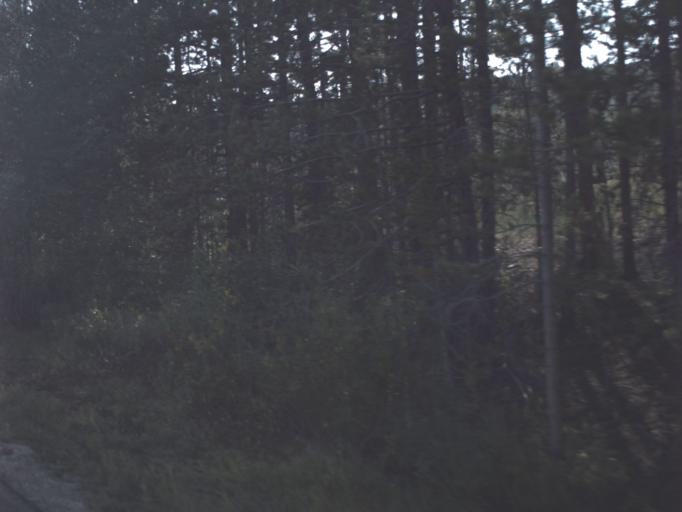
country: US
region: Wyoming
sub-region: Uinta County
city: Evanston
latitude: 40.8599
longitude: -110.8417
